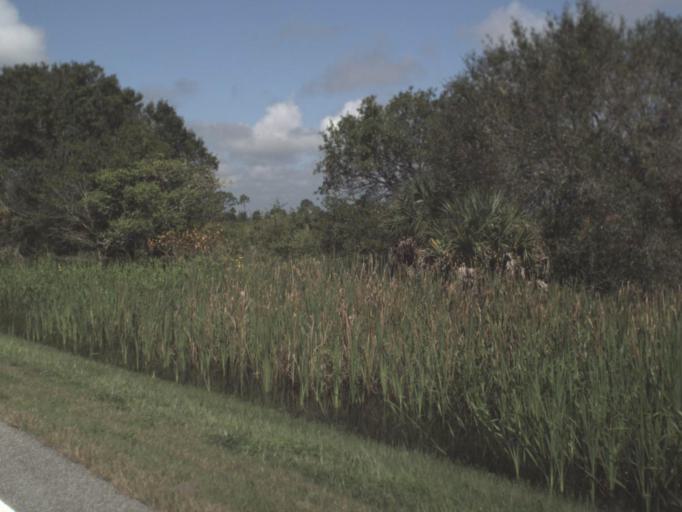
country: US
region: Florida
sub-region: Sarasota County
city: Warm Mineral Springs
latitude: 27.2188
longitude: -82.2809
